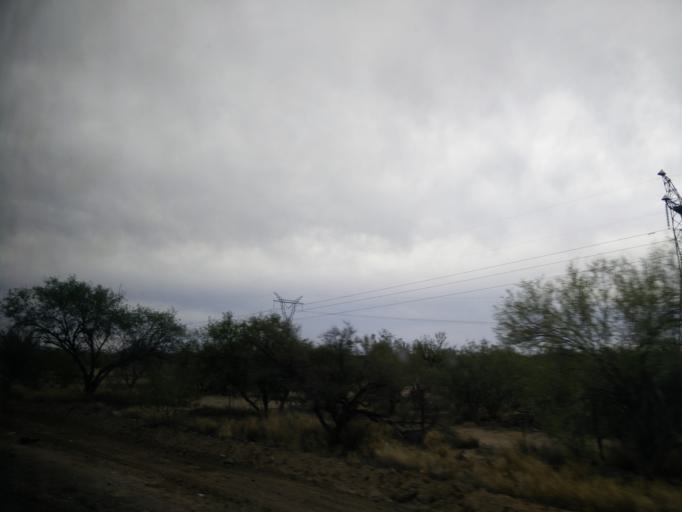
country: MX
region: Sonora
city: Hermosillo
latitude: 28.6743
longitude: -110.9942
